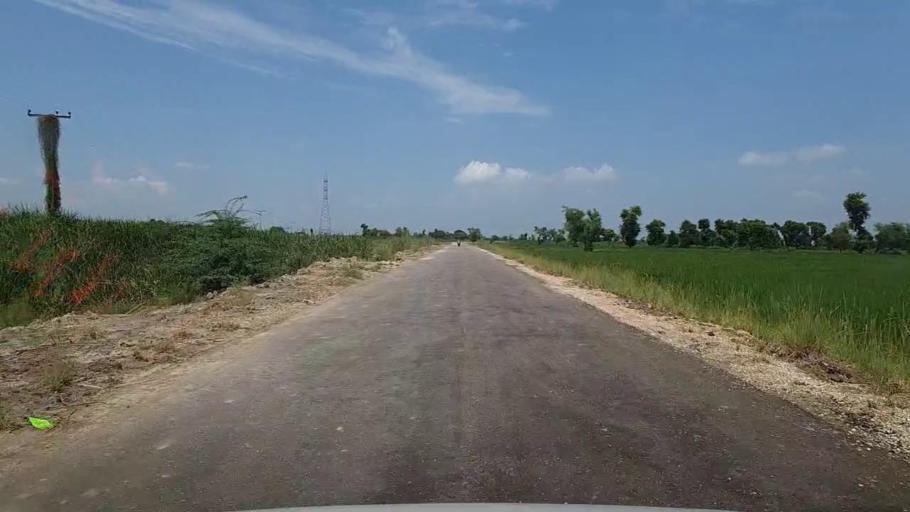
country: PK
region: Sindh
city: Bhiria
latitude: 26.9218
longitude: 68.2078
